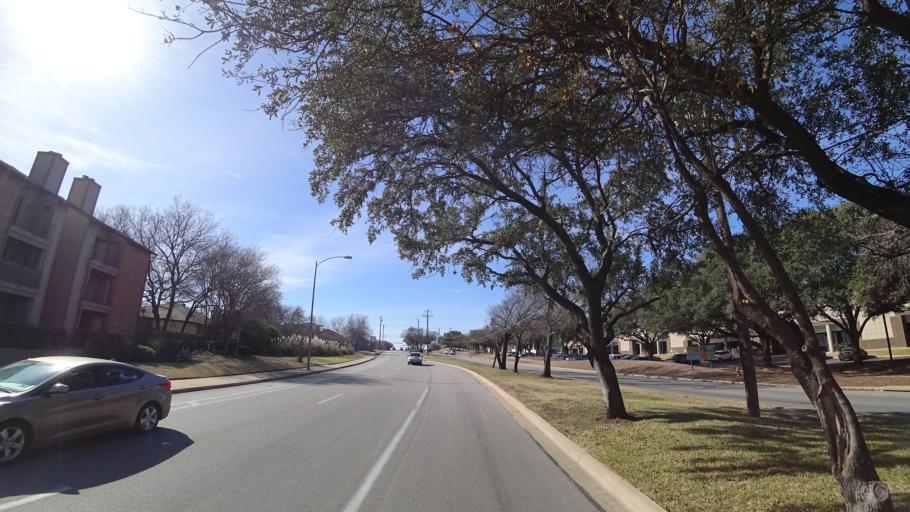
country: US
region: Texas
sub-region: Travis County
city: Wells Branch
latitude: 30.3945
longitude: -97.7068
